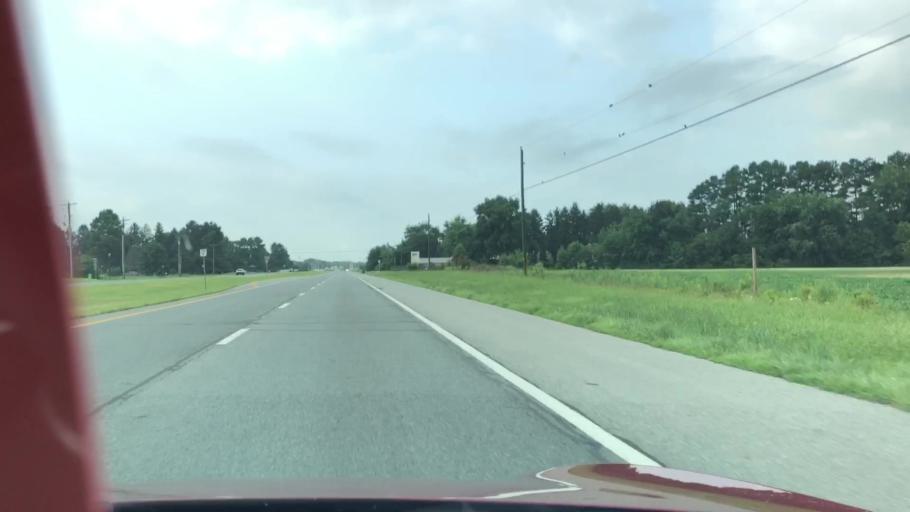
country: US
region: Delaware
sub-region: Kent County
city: Woodside East
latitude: 39.0564
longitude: -75.5559
